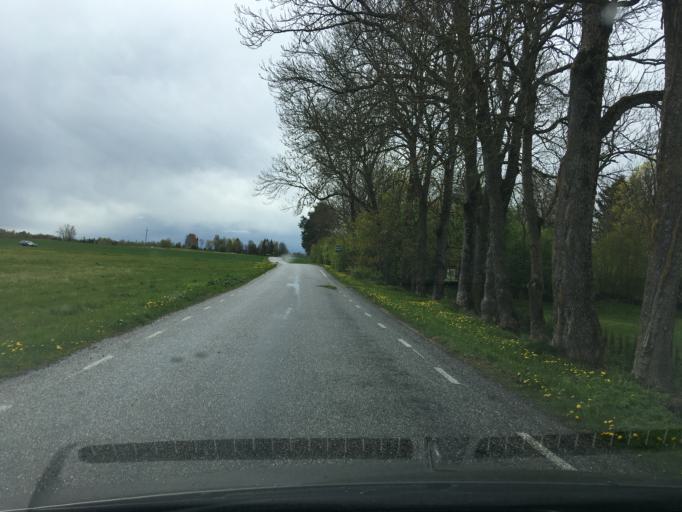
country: EE
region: Harju
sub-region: Joelaehtme vald
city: Loo
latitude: 59.4249
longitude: 24.9896
